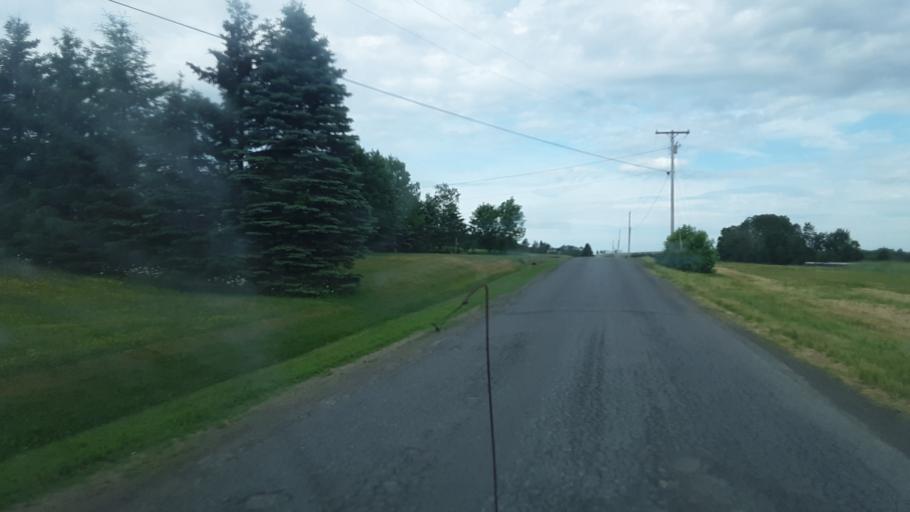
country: US
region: Maine
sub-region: Aroostook County
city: Caribou
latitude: 46.8112
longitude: -68.0151
